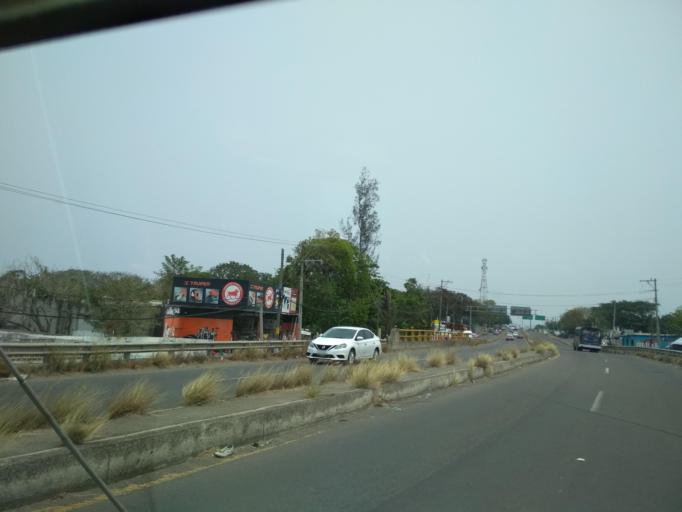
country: MX
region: Veracruz
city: Paso del Toro
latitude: 19.0331
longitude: -96.1382
